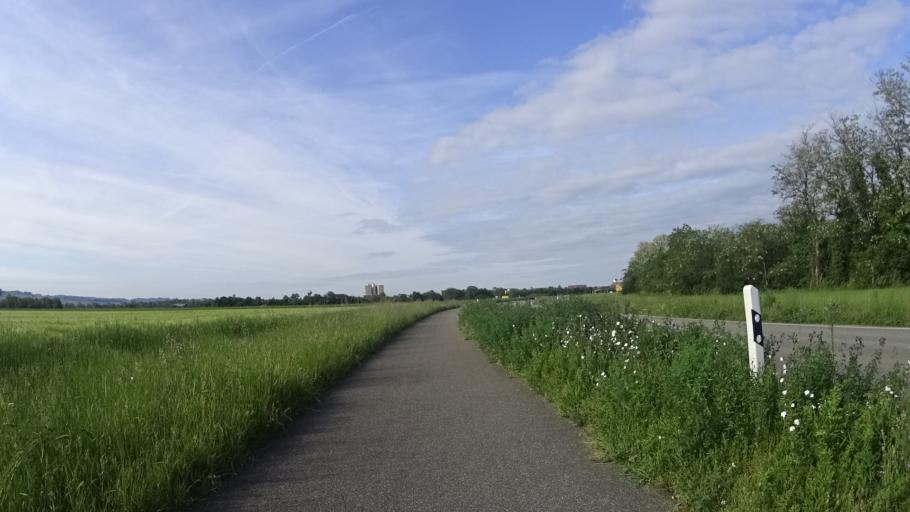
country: DE
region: Baden-Wuerttemberg
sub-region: Freiburg Region
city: Neuenburg am Rhein
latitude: 47.8239
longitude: 7.5742
